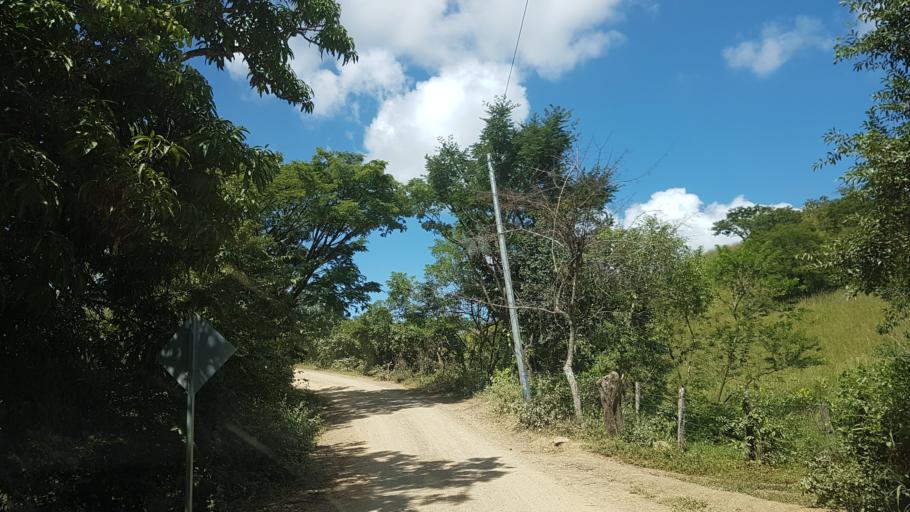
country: HN
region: El Paraiso
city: Santa Cruz
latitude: 13.7323
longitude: -86.6913
